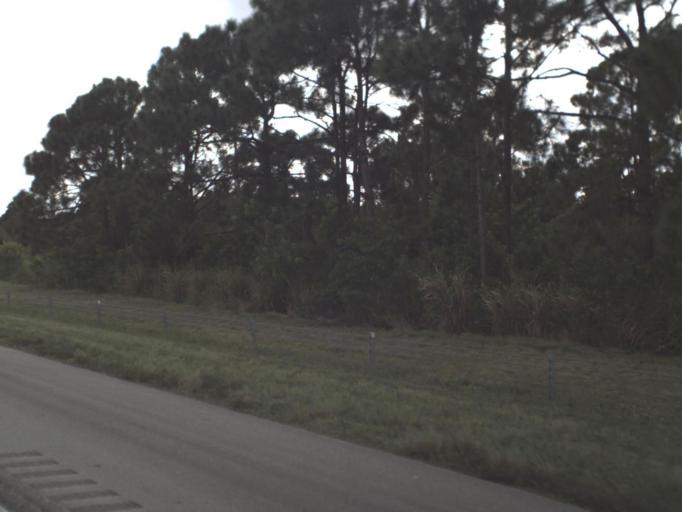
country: US
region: Florida
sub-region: Saint Lucie County
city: River Park
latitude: 27.3302
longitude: -80.3744
